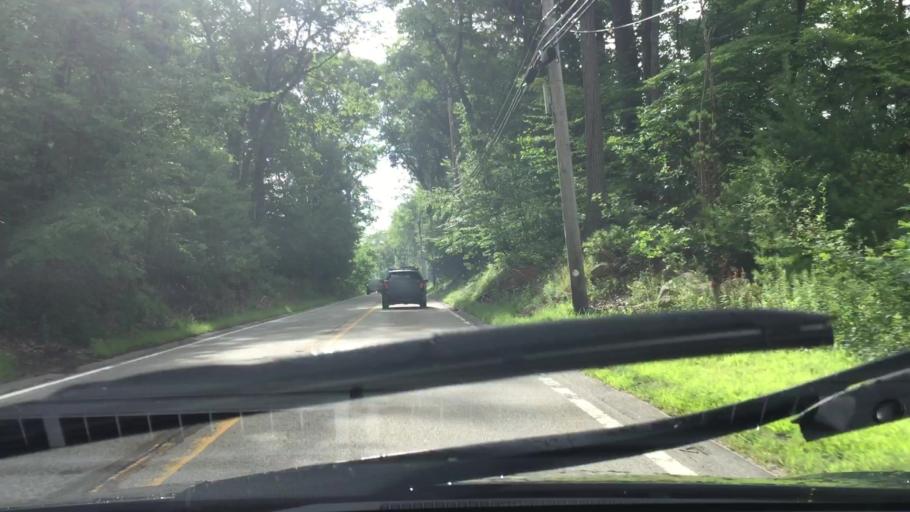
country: US
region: Massachusetts
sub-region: Middlesex County
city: Stow
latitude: 42.4834
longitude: -71.5256
